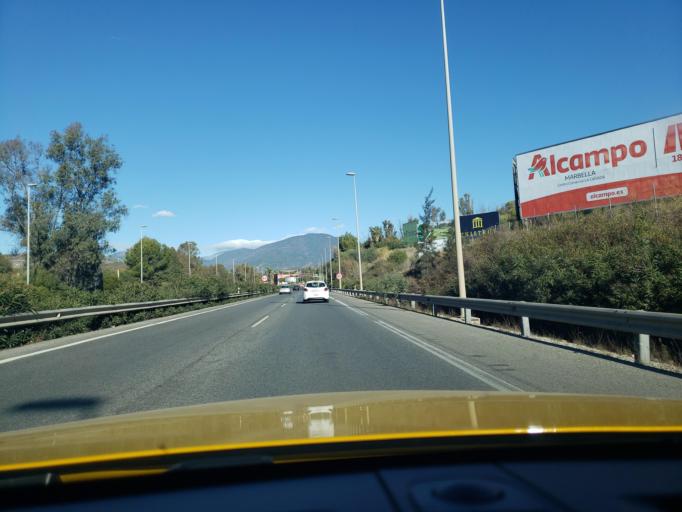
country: ES
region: Andalusia
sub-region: Provincia de Malaga
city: Marbella
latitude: 36.5056
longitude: -4.9477
